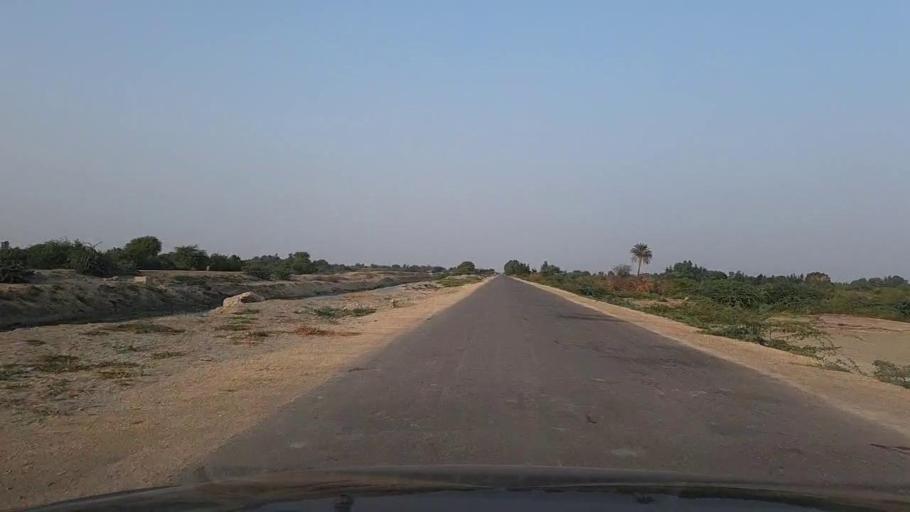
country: PK
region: Sindh
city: Mirpur Sakro
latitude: 24.4938
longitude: 67.8109
